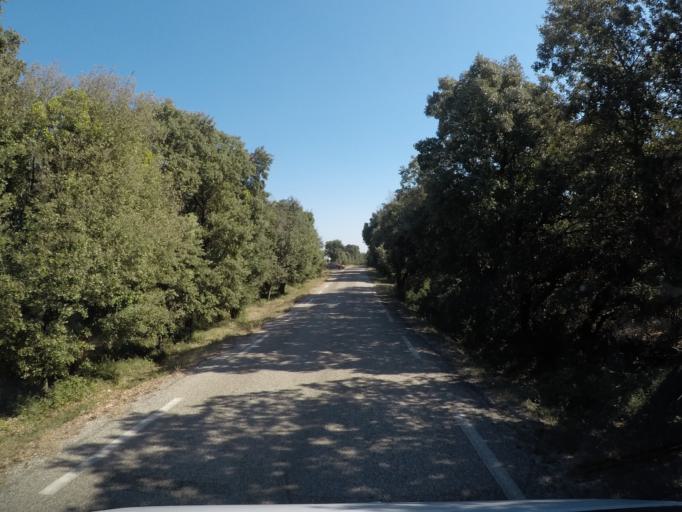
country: FR
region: Languedoc-Roussillon
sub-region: Departement du Gard
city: Saint-Victor-la-Coste
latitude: 44.0172
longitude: 4.6246
